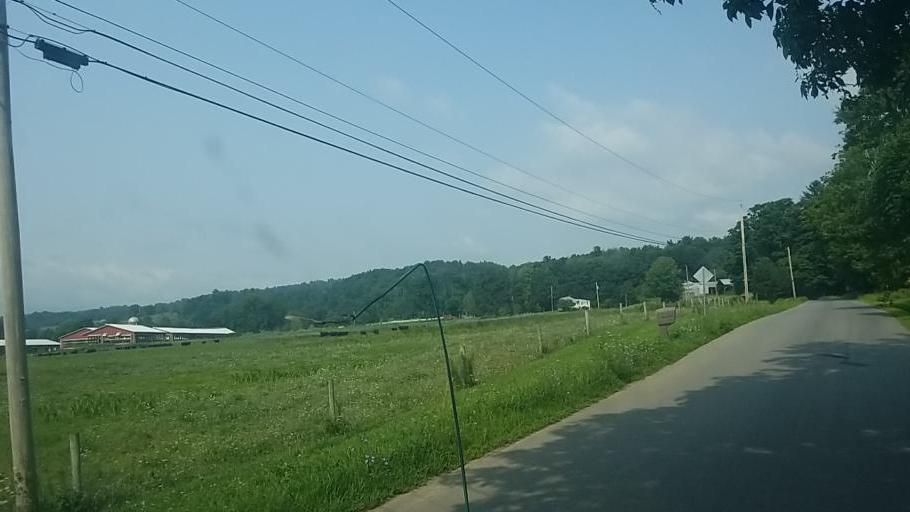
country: US
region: New York
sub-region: Montgomery County
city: Fonda
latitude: 42.9487
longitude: -74.4326
